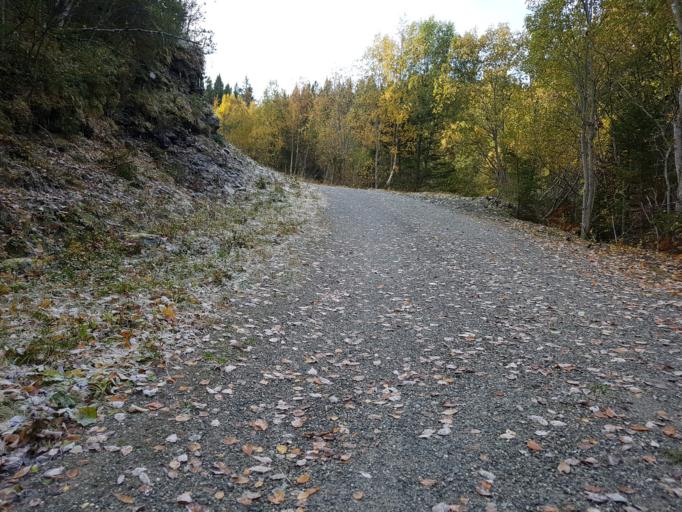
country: NO
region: Sor-Trondelag
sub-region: Trondheim
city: Trondheim
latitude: 63.4496
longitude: 10.2905
